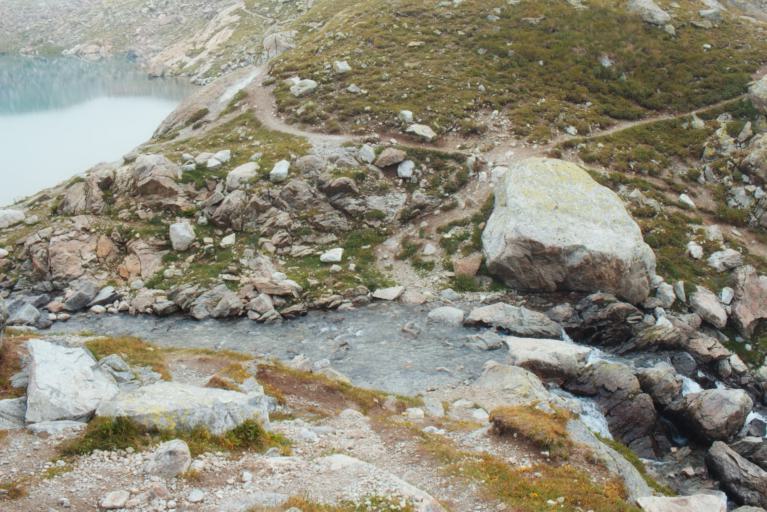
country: RU
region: Karachayevo-Cherkesiya
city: Nizhniy Arkhyz
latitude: 43.4496
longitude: 41.2326
